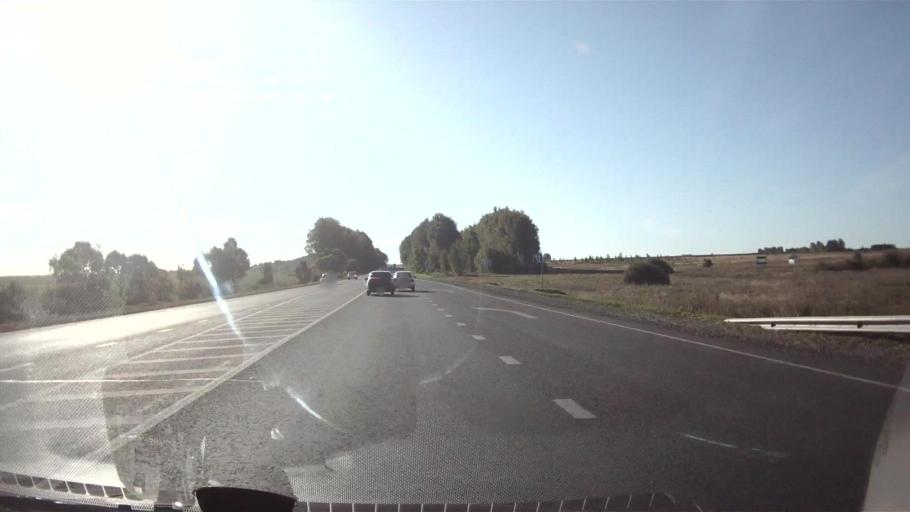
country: RU
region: Chuvashia
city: Shikhazany
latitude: 55.5497
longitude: 47.4184
